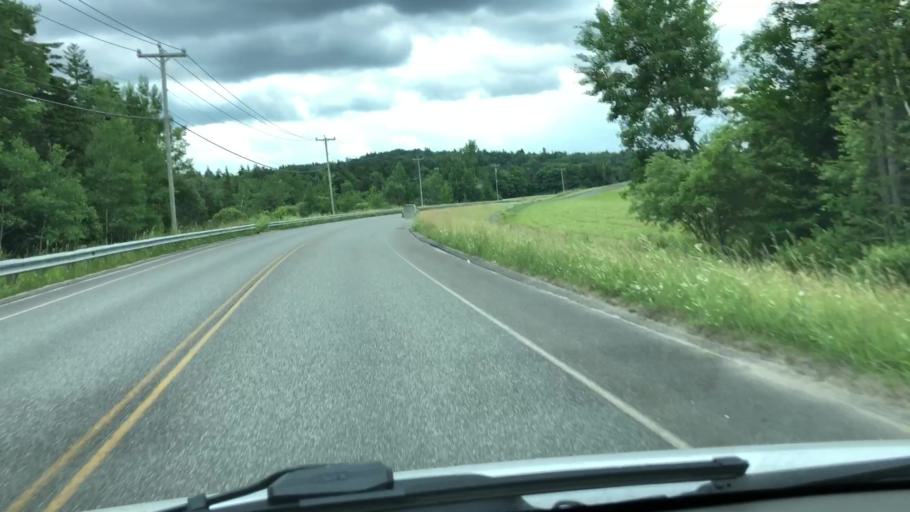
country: US
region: Massachusetts
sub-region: Berkshire County
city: Adams
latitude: 42.5317
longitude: -73.0565
